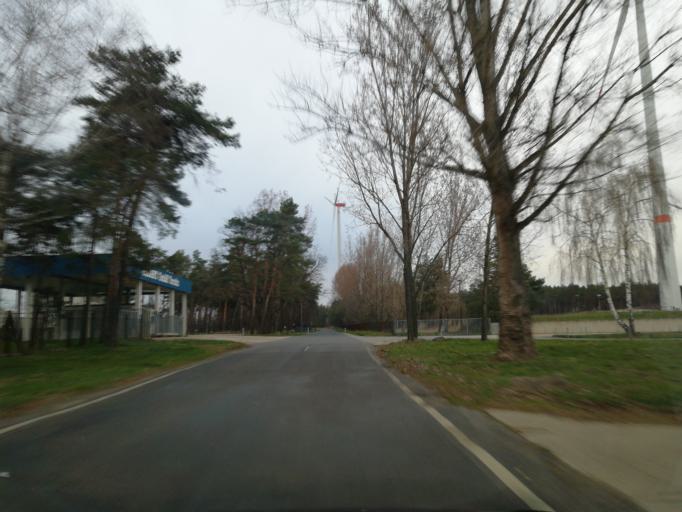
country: DE
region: Brandenburg
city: Vetschau
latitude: 51.7511
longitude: 14.0940
